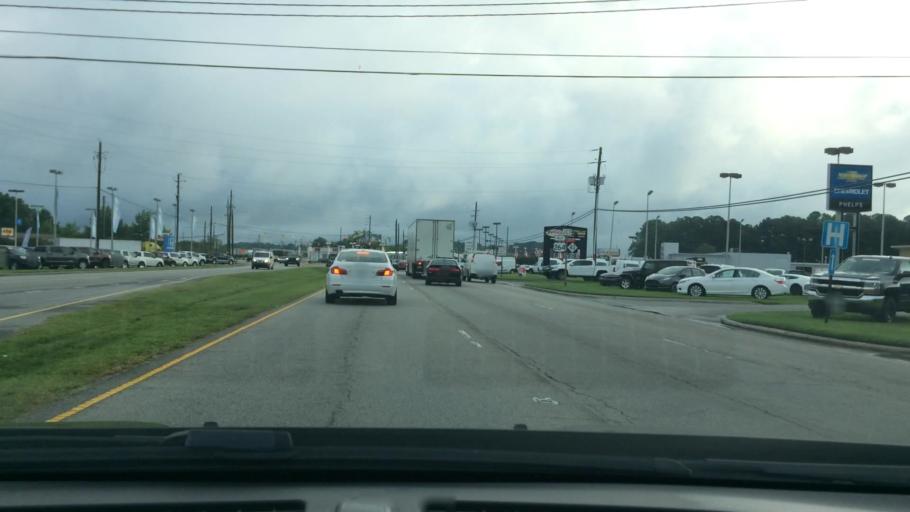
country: US
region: North Carolina
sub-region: Pitt County
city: Summerfield
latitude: 35.5702
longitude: -77.4042
